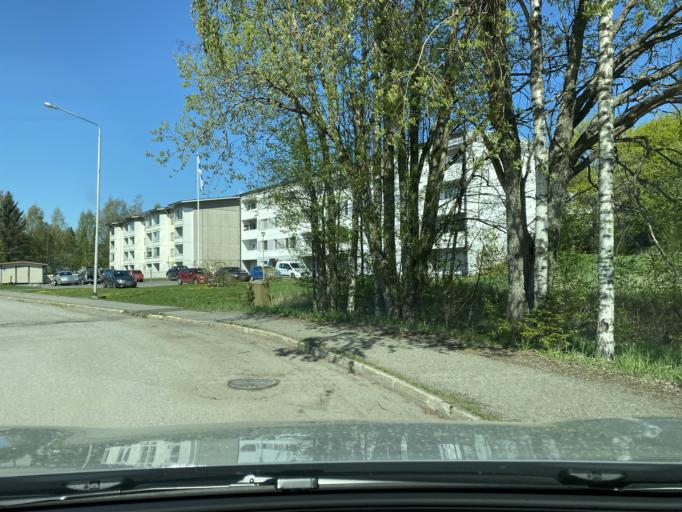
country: FI
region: Pirkanmaa
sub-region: Lounais-Pirkanmaa
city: Vammala
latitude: 61.3477
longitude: 22.8929
